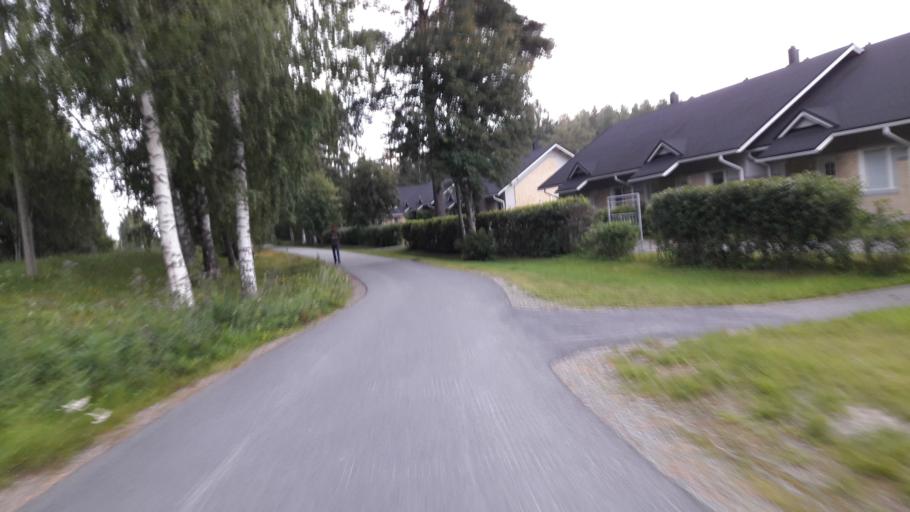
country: FI
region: North Karelia
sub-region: Joensuu
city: Joensuu
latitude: 62.5464
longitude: 29.8317
